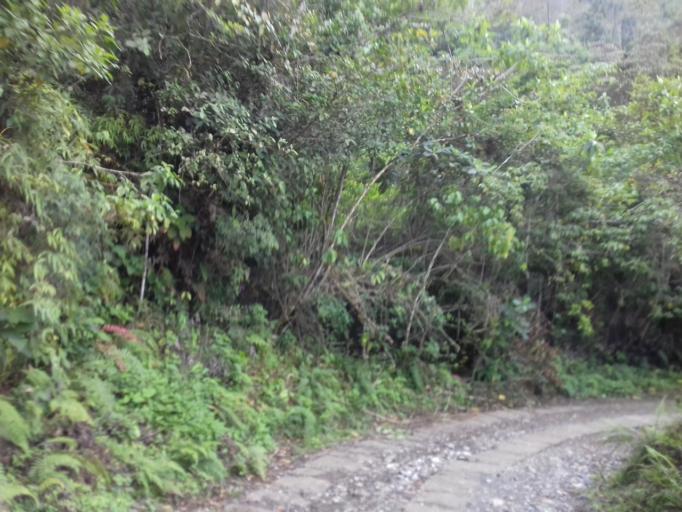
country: CO
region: Tolima
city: Libano
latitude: 4.9435
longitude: -75.0550
